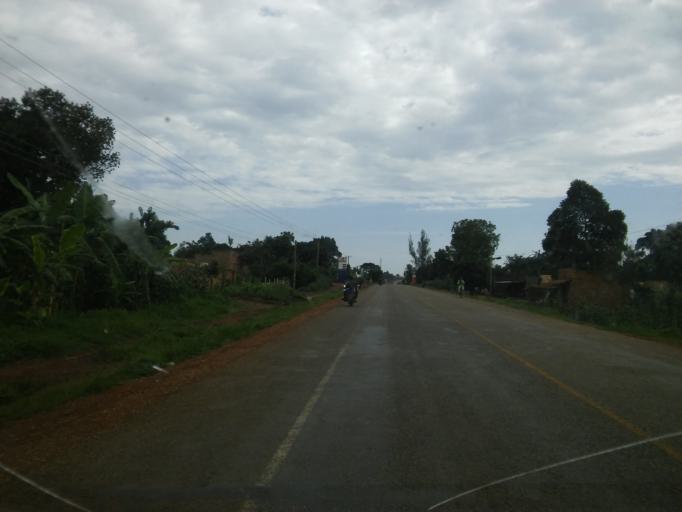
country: UG
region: Eastern Region
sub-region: Mbale District
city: Mbale
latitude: 1.1302
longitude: 34.1670
